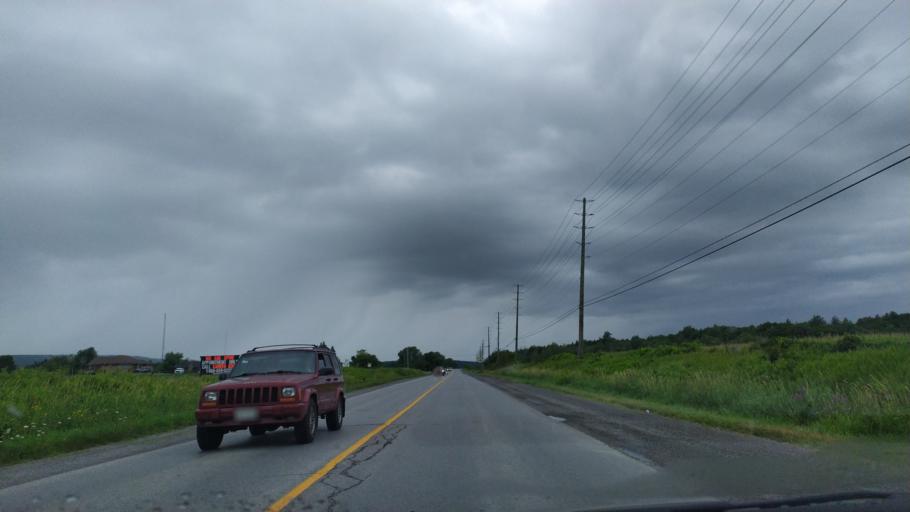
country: CA
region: Ontario
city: Quinte West
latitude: 44.0937
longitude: -77.6135
